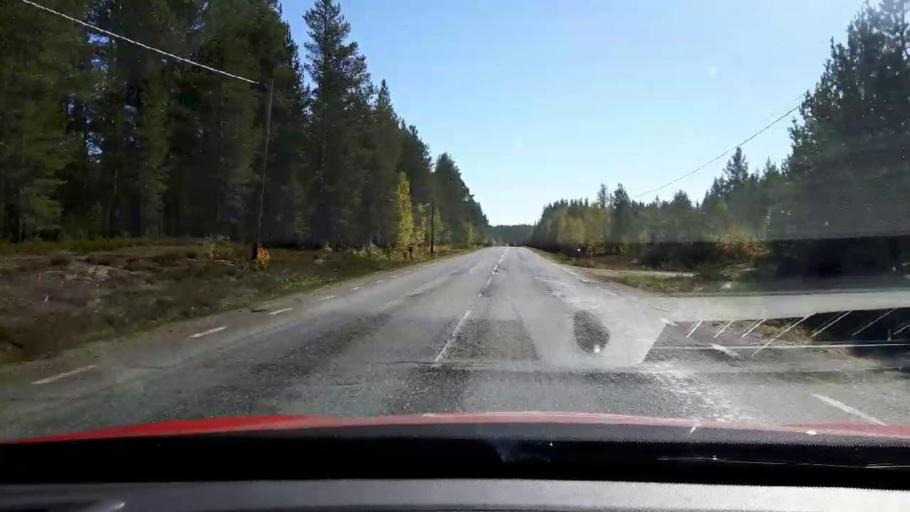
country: SE
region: Jaemtland
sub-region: Harjedalens Kommun
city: Sveg
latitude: 62.3386
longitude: 14.0426
